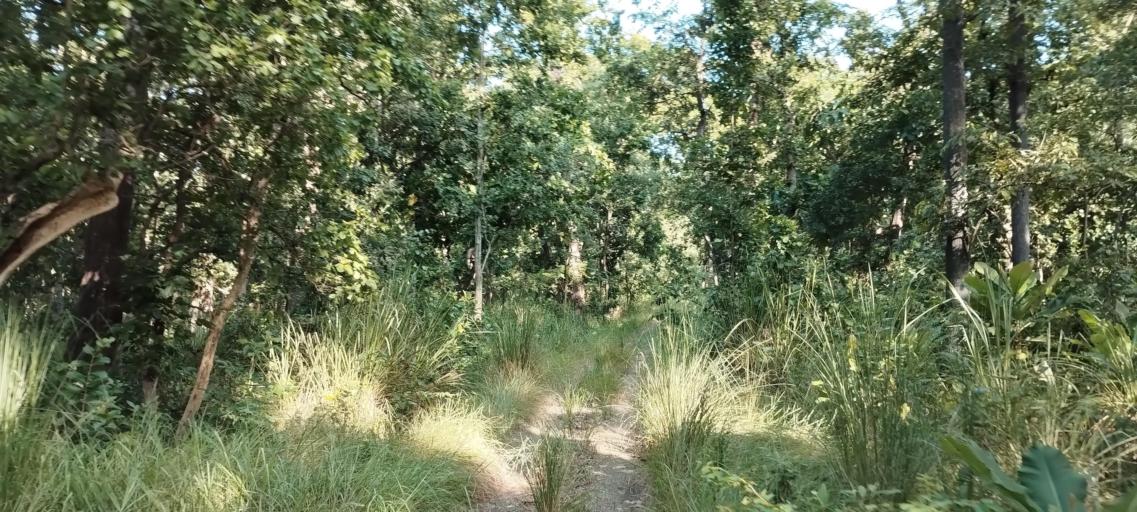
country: NP
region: Far Western
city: Tikapur
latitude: 28.5221
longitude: 81.2710
